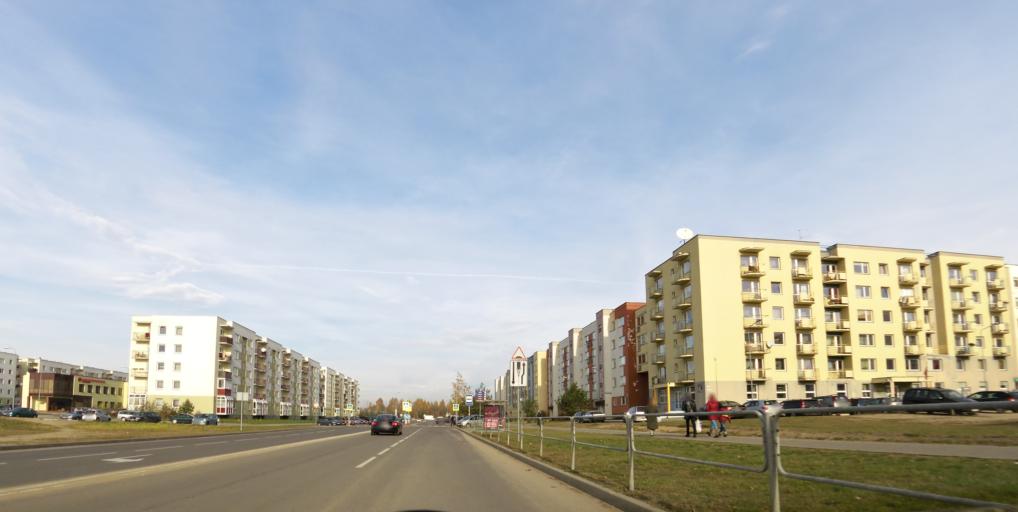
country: LT
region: Vilnius County
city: Pilaite
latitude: 54.7076
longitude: 25.1751
